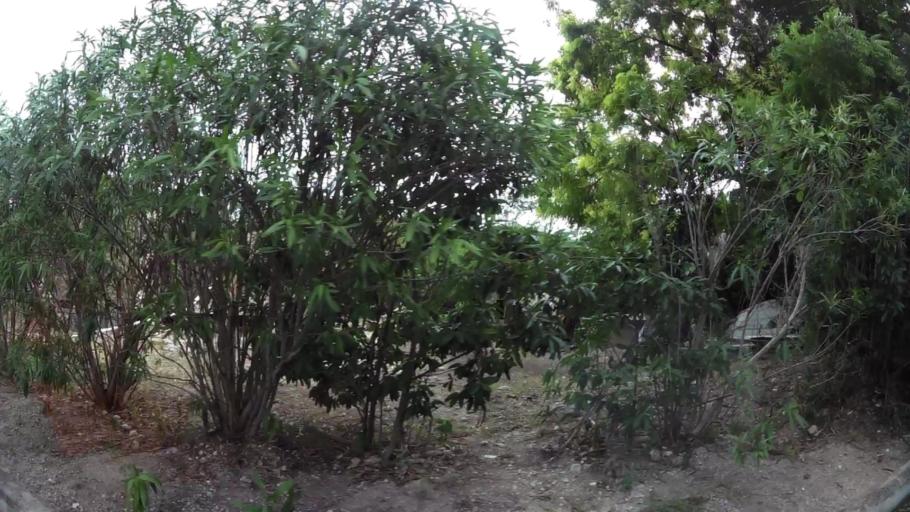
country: AG
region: Saint Paul
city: Falmouth
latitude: 17.0457
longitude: -61.6988
